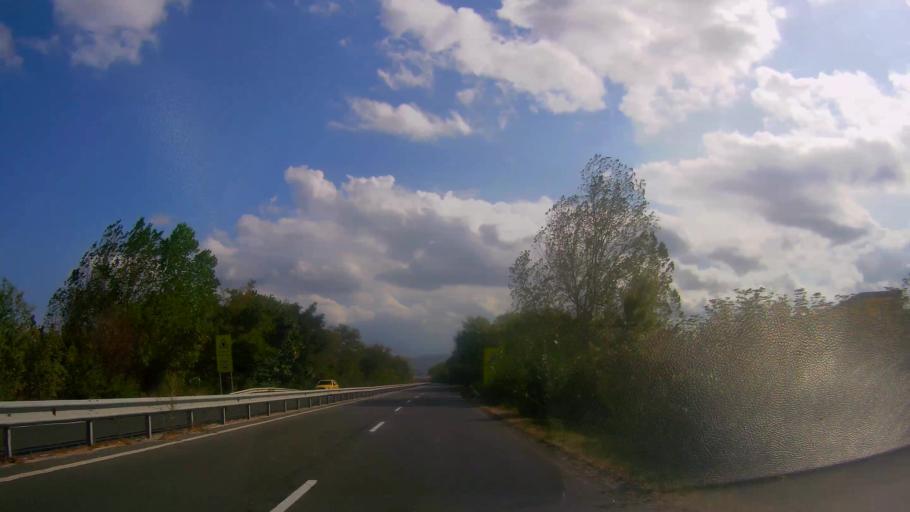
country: BG
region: Burgas
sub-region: Obshtina Sozopol
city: Chernomorets
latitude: 42.4367
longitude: 27.6371
